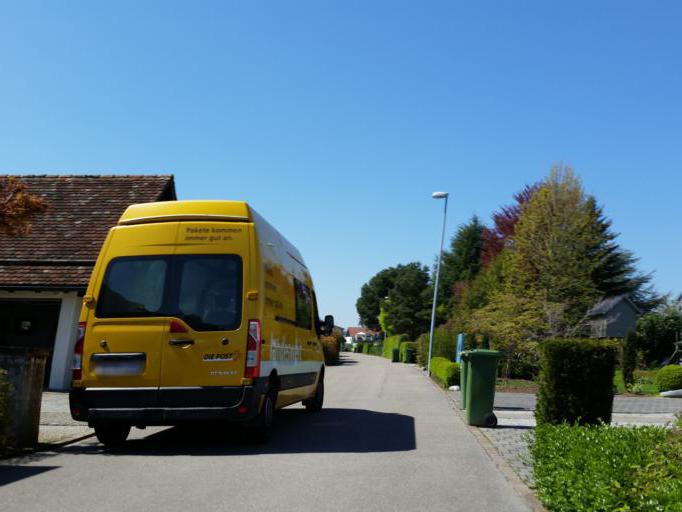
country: CH
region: Thurgau
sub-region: Arbon District
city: Romanshorn
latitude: 47.5736
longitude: 9.3708
